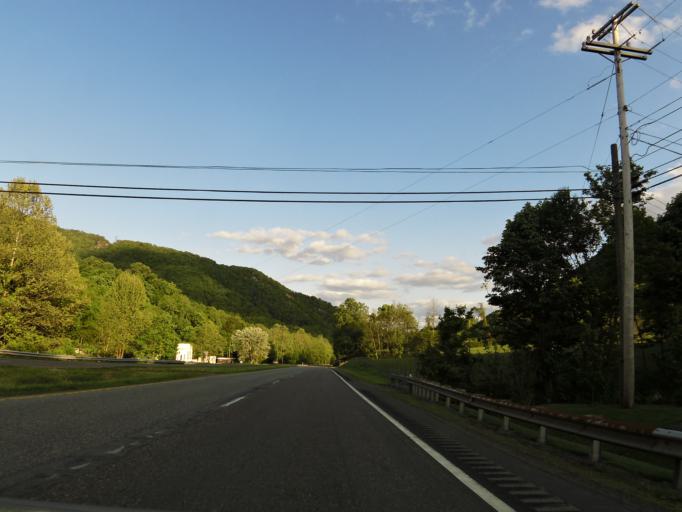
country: US
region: Virginia
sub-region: Russell County
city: Lebanon
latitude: 36.8085
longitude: -82.0995
